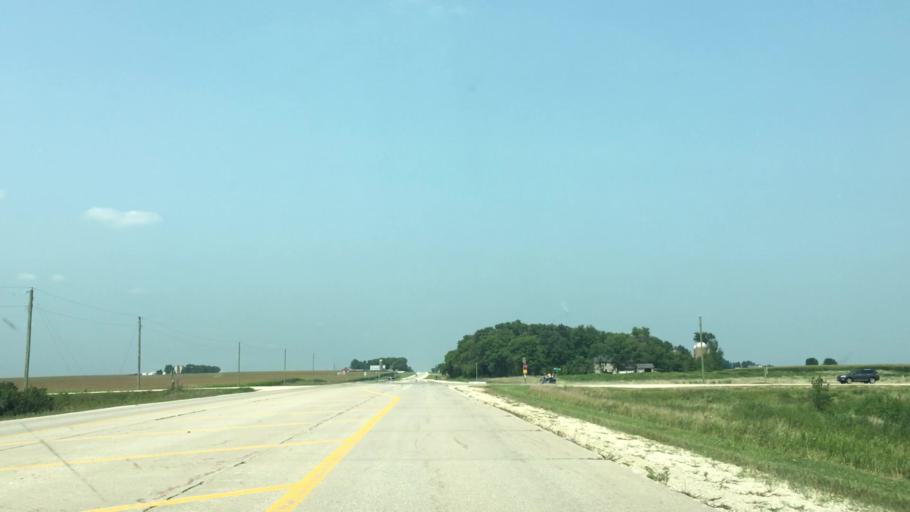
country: US
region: Iowa
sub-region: Fayette County
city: Fayette
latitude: 42.7591
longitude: -91.8043
